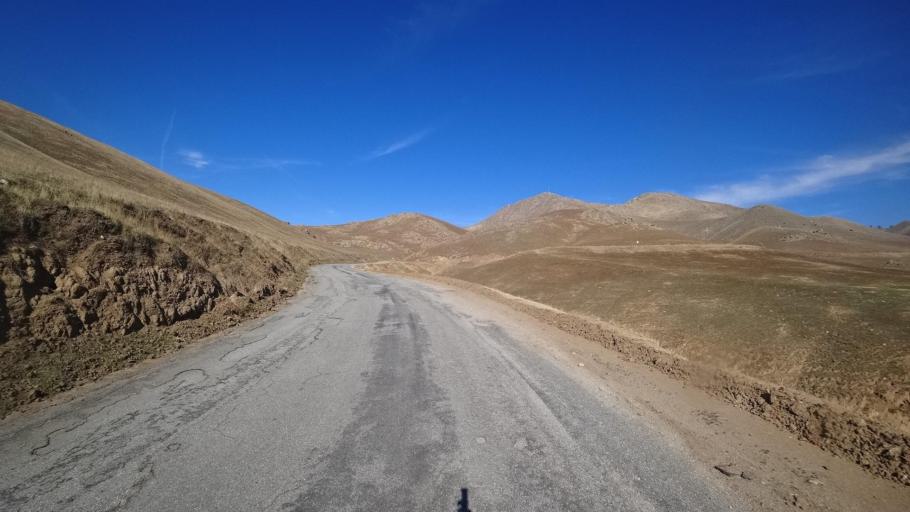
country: US
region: California
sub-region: Kern County
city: Arvin
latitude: 35.4157
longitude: -118.7475
